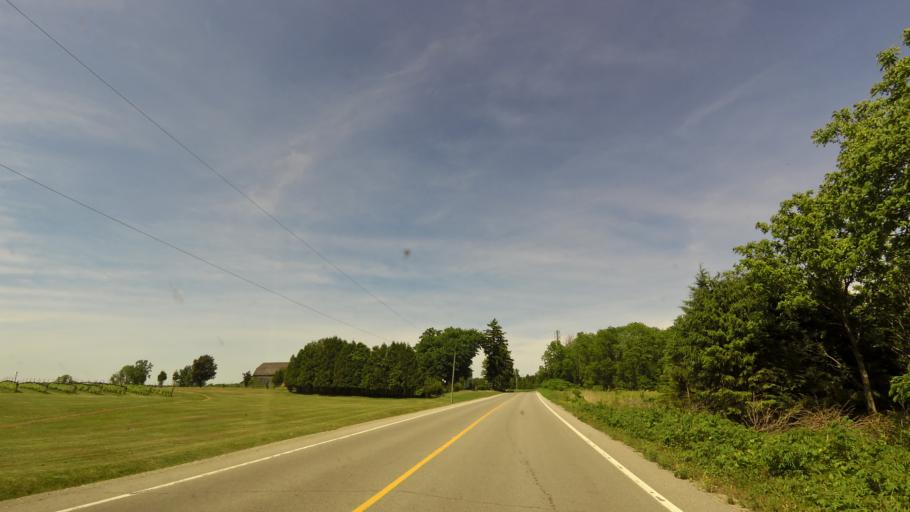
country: CA
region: Ontario
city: Norfolk County
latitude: 42.6905
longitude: -80.3499
